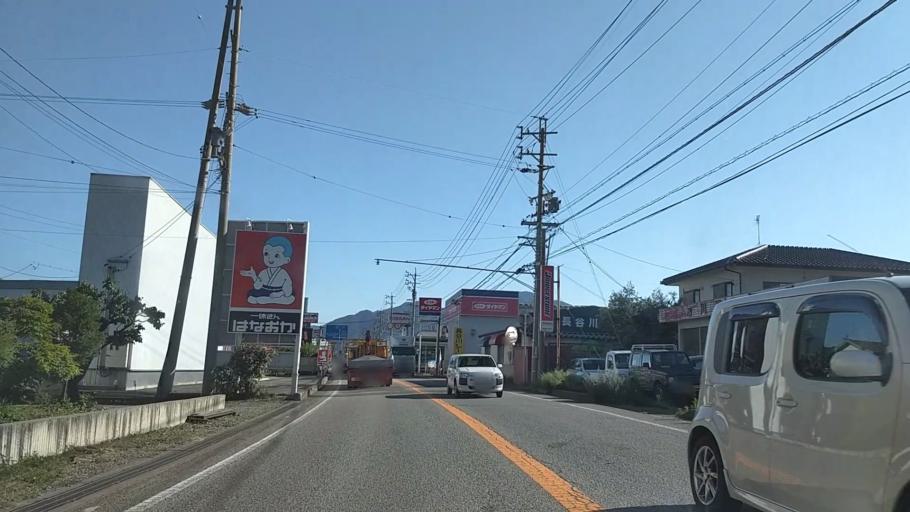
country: JP
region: Nagano
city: Nagano-shi
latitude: 36.5399
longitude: 138.1225
